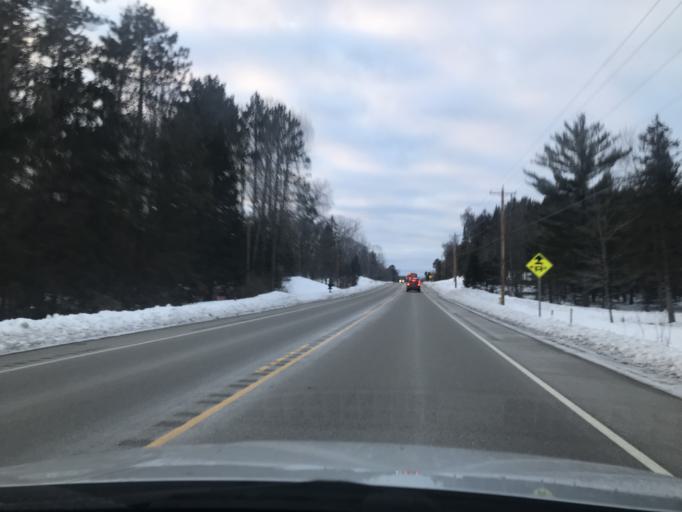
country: US
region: Wisconsin
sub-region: Marinette County
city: Marinette
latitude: 45.1574
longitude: -87.7158
